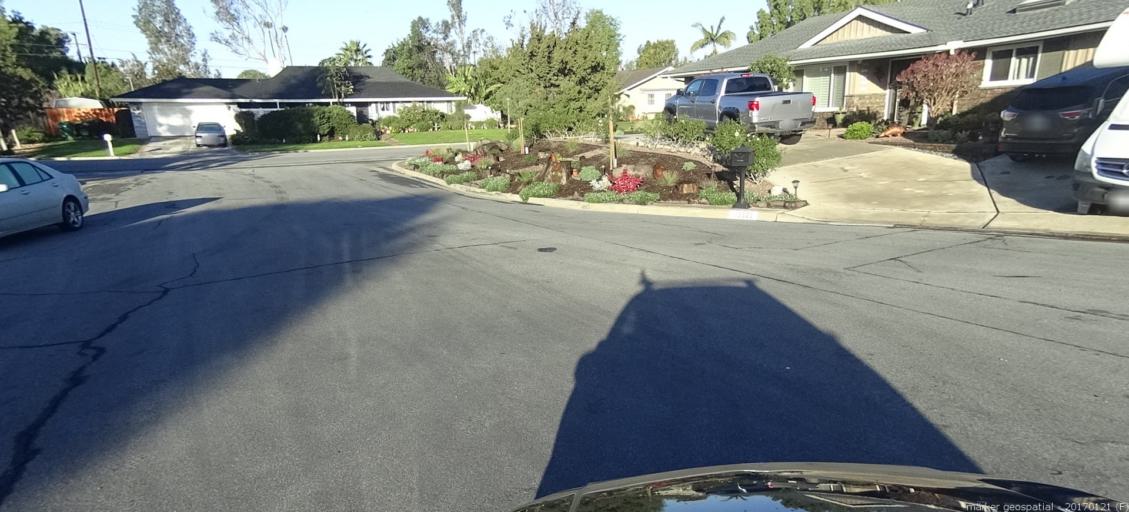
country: US
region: California
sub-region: Orange County
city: North Tustin
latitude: 33.7686
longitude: -117.8100
